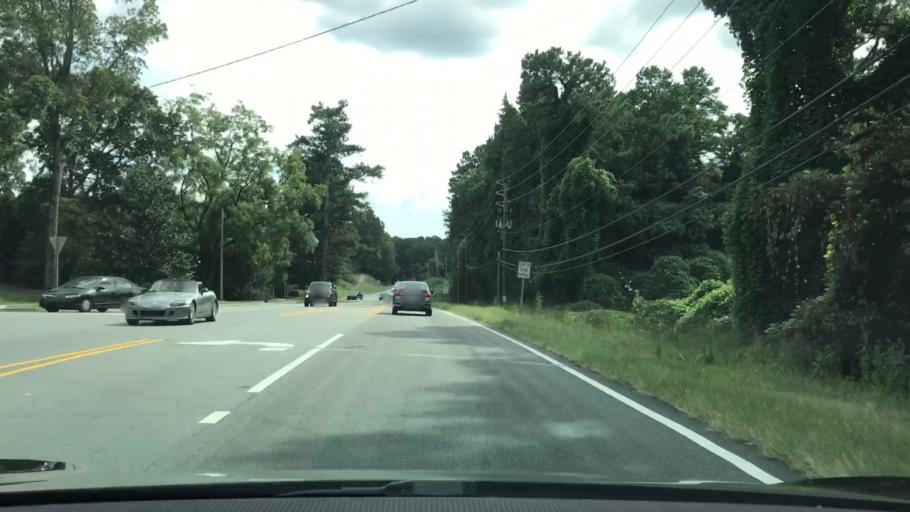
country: US
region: Georgia
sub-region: Gwinnett County
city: Suwanee
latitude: 34.0679
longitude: -84.0585
